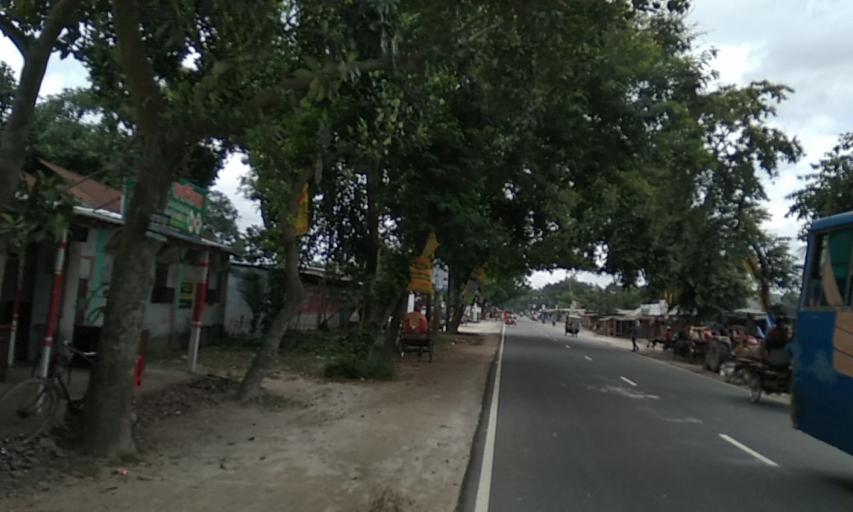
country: BD
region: Rangpur Division
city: Rangpur
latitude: 25.7999
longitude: 89.1906
